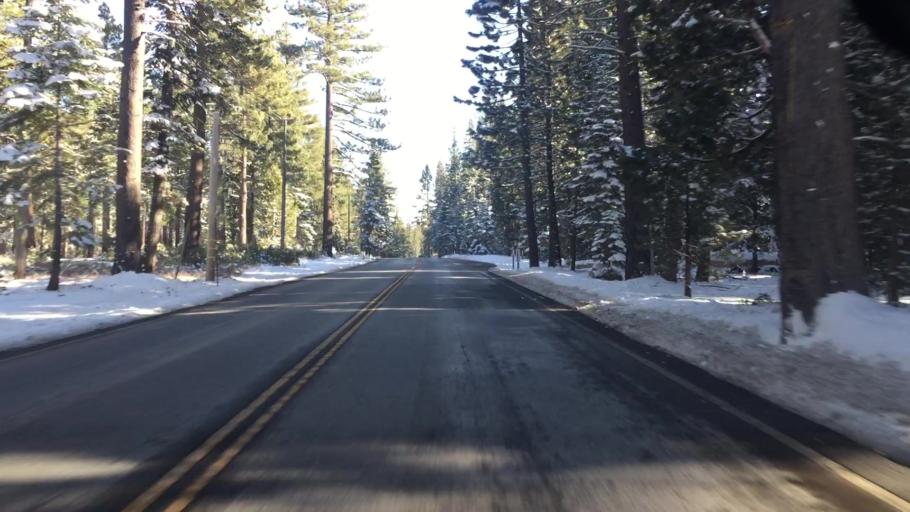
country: US
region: California
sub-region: Placer County
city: Tahoma
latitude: 39.0568
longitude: -120.1195
